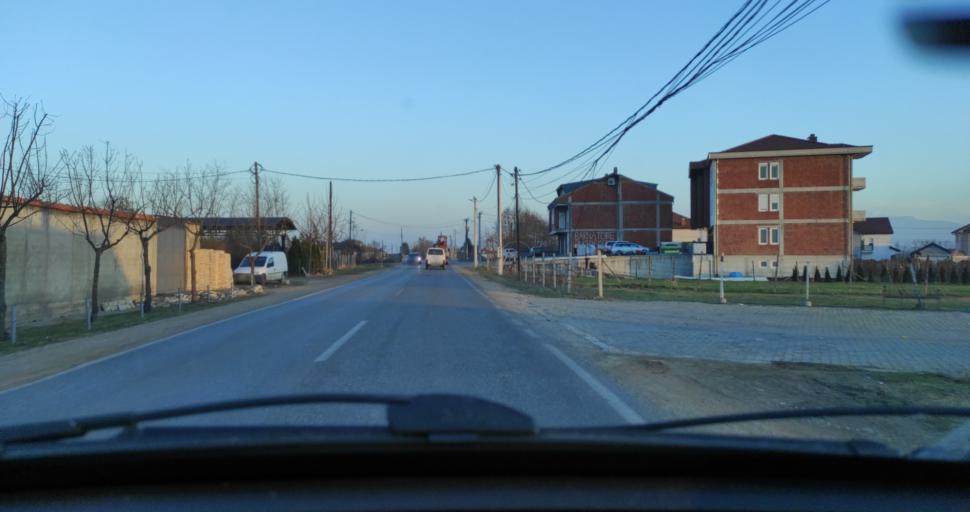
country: XK
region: Gjakova
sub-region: Komuna e Decanit
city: Gllogjan
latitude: 42.4345
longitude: 20.3765
